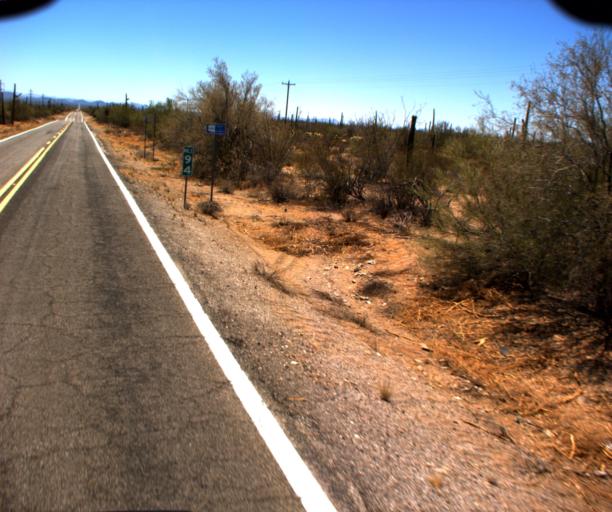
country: US
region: Arizona
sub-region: Pima County
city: Sells
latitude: 32.1377
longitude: -112.0958
